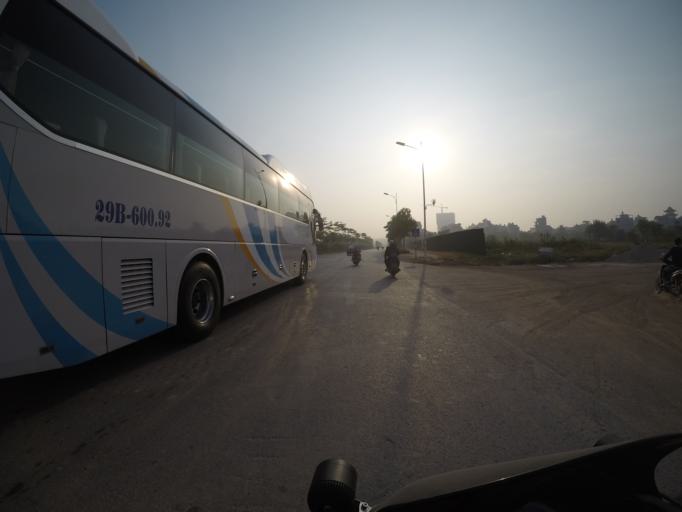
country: VN
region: Ha Noi
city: Hoan Kiem
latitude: 21.0288
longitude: 105.8897
